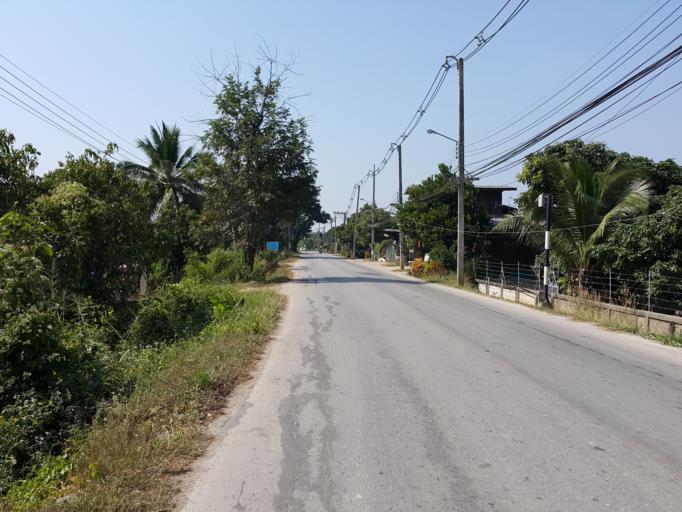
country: TH
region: Lamphun
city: Pa Sang
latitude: 18.5379
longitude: 98.9333
